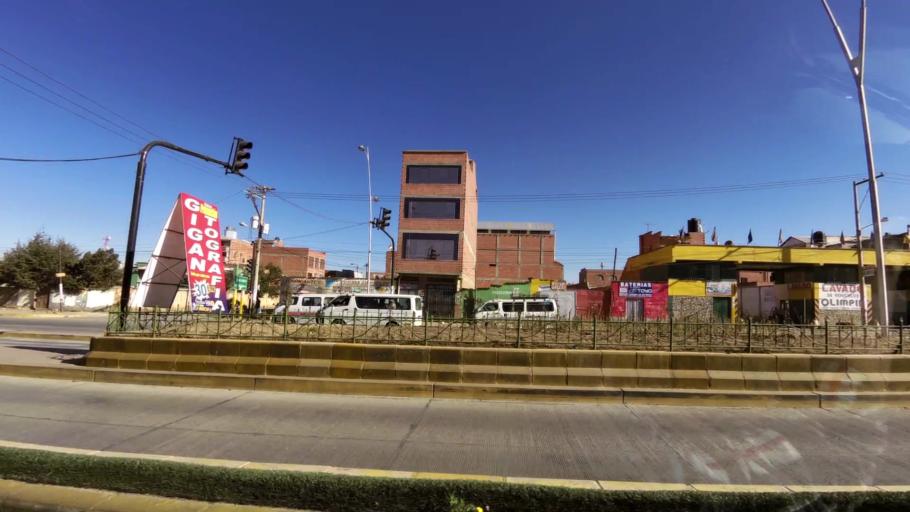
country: BO
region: La Paz
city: La Paz
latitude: -16.5254
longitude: -68.1821
